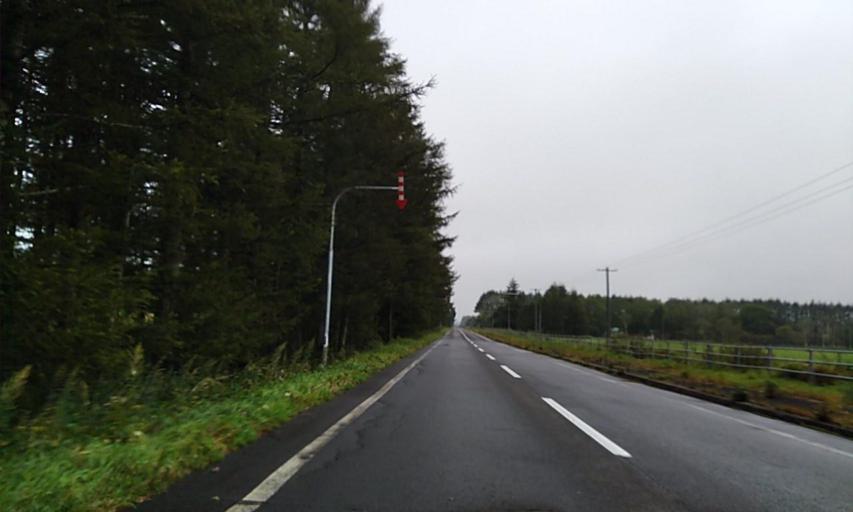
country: JP
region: Hokkaido
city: Shibetsu
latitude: 43.4975
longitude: 144.6509
